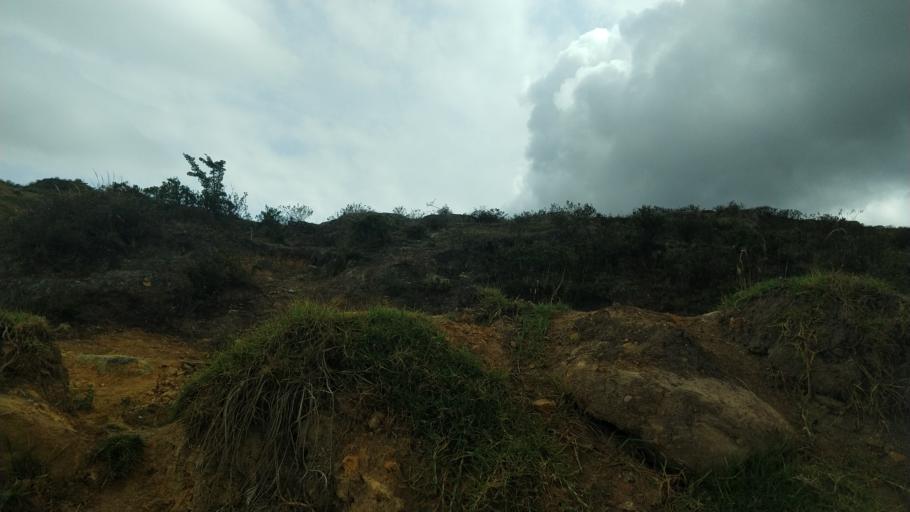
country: CO
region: Cundinamarca
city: Soacha
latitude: 4.5615
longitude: -74.1884
